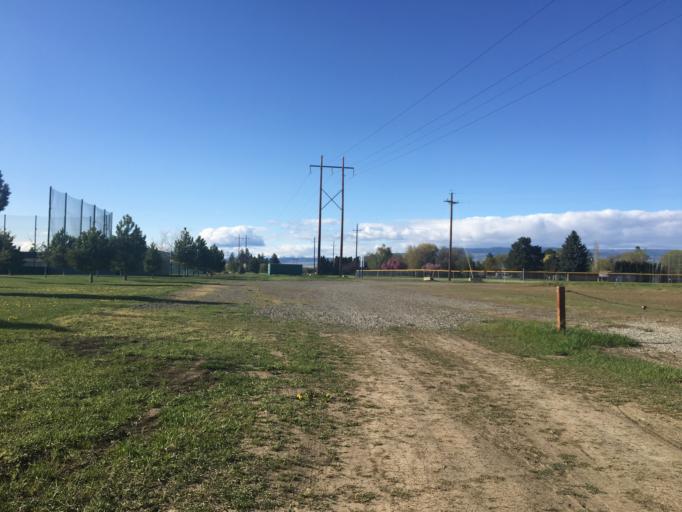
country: US
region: Washington
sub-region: Kittitas County
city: Ellensburg
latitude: 46.9910
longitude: -120.5609
